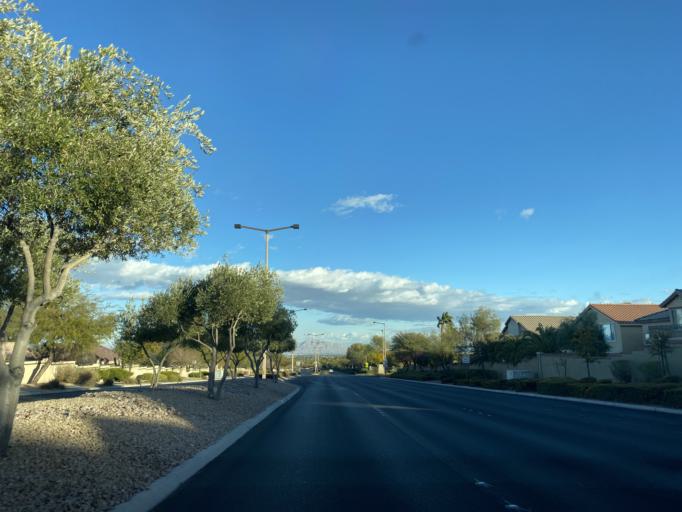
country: US
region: Nevada
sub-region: Clark County
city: Summerlin South
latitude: 36.2047
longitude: -115.3160
